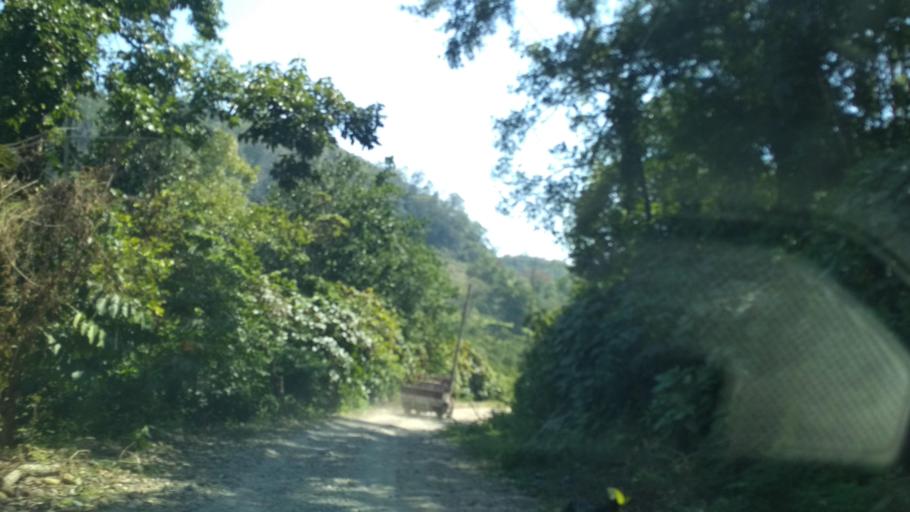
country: MX
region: Veracruz
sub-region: Papantla
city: Polutla
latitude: 20.4753
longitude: -97.2188
